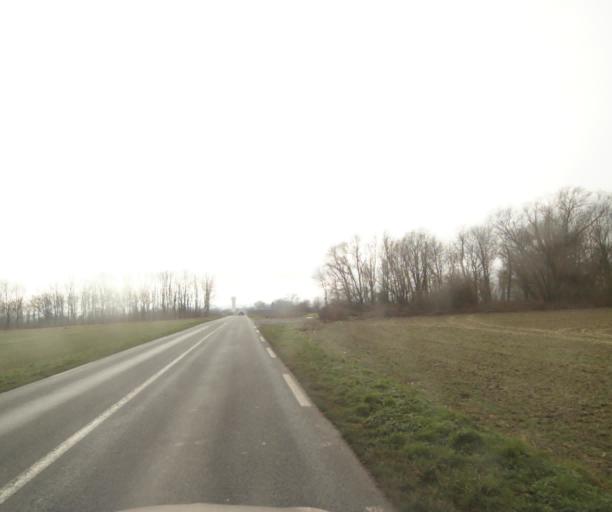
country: FR
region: Nord-Pas-de-Calais
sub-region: Departement du Nord
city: Vendegies-sur-Ecaillon
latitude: 50.2783
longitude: 3.5161
